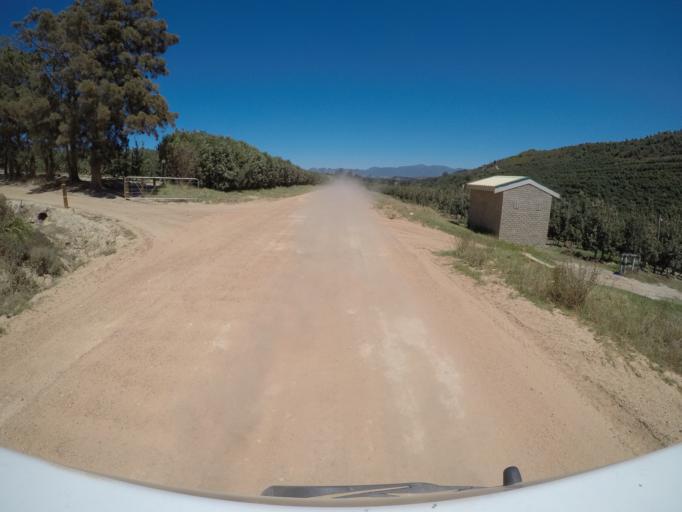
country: ZA
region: Western Cape
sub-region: Overberg District Municipality
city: Grabouw
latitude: -34.2446
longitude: 19.1063
